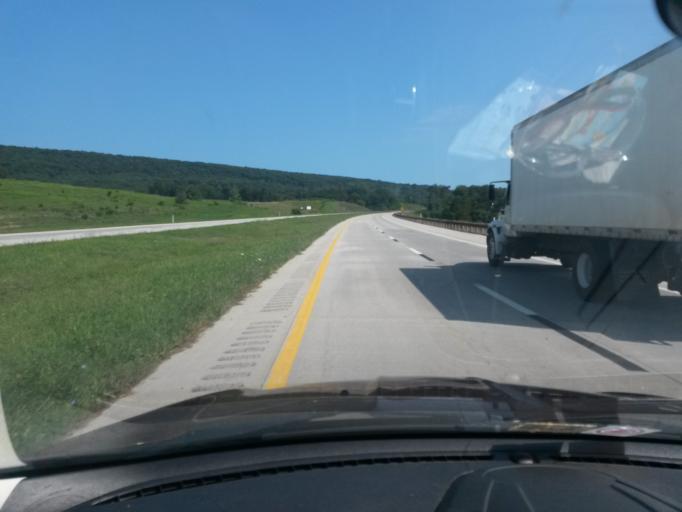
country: US
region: West Virginia
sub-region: Hardy County
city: Moorefield
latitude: 39.0969
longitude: -78.9859
